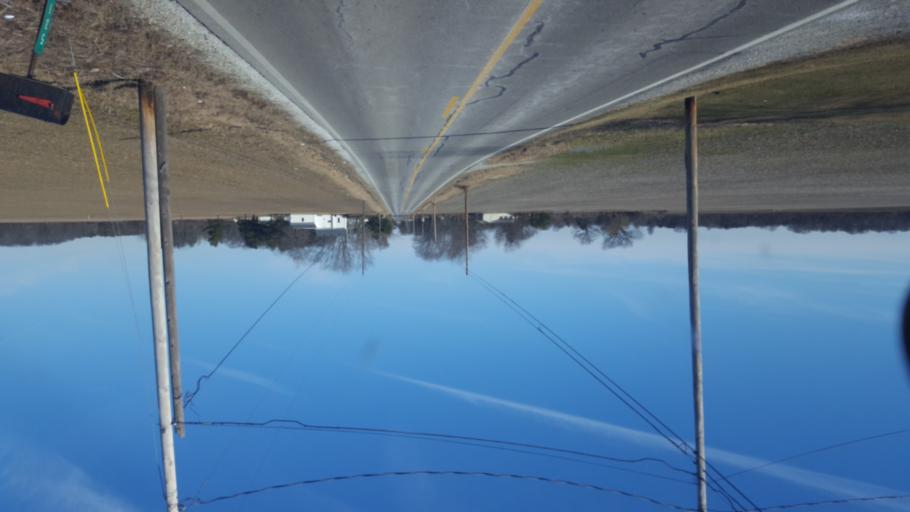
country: US
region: Ohio
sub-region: Marion County
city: Marion
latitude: 40.5348
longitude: -83.1226
